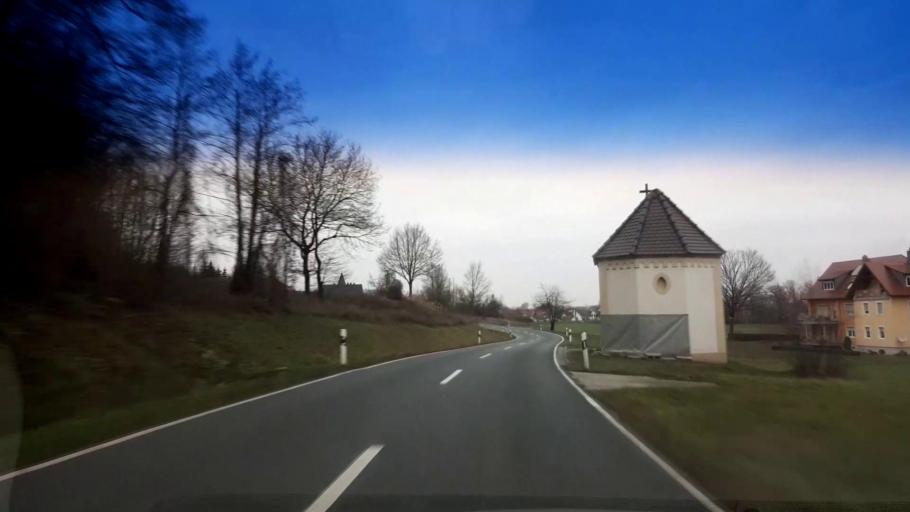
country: DE
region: Bavaria
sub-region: Upper Franconia
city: Altendorf
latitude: 49.7867
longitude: 11.0056
